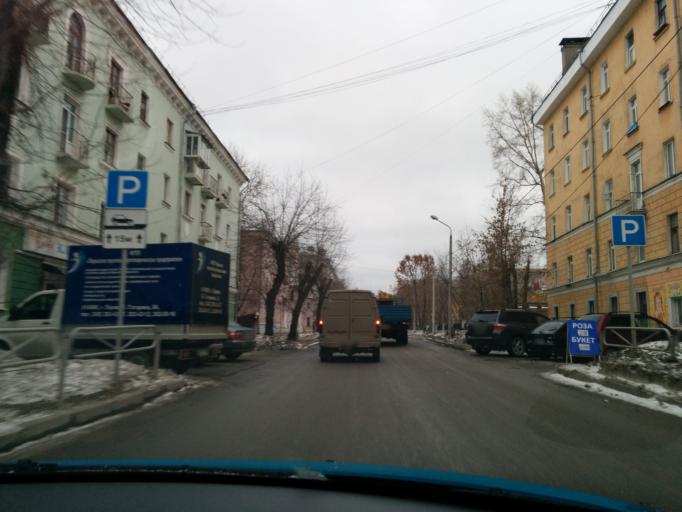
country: RU
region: Perm
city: Perm
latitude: 58.0209
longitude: 56.2825
